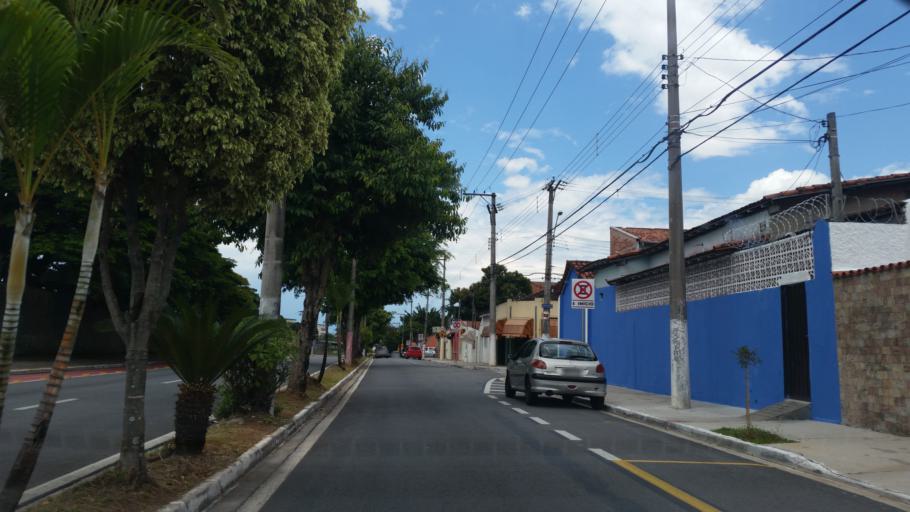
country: BR
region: Sao Paulo
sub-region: Taubate
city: Taubate
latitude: -23.0223
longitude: -45.5779
